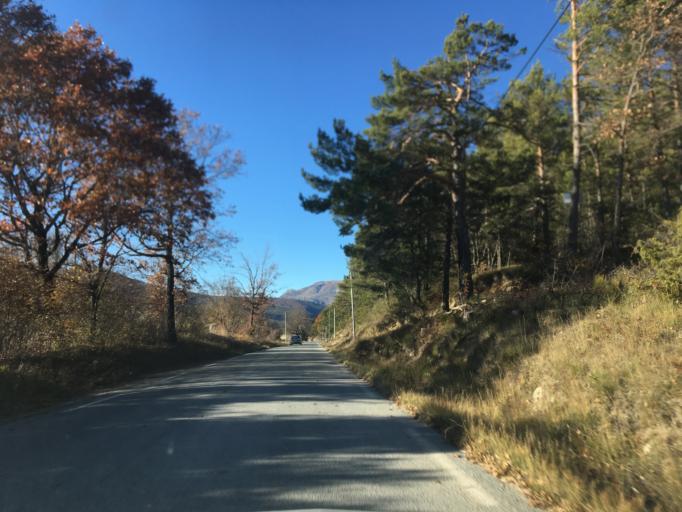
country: FR
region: Provence-Alpes-Cote d'Azur
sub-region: Departement des Alpes-de-Haute-Provence
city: Castellane
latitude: 43.7519
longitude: 6.4682
